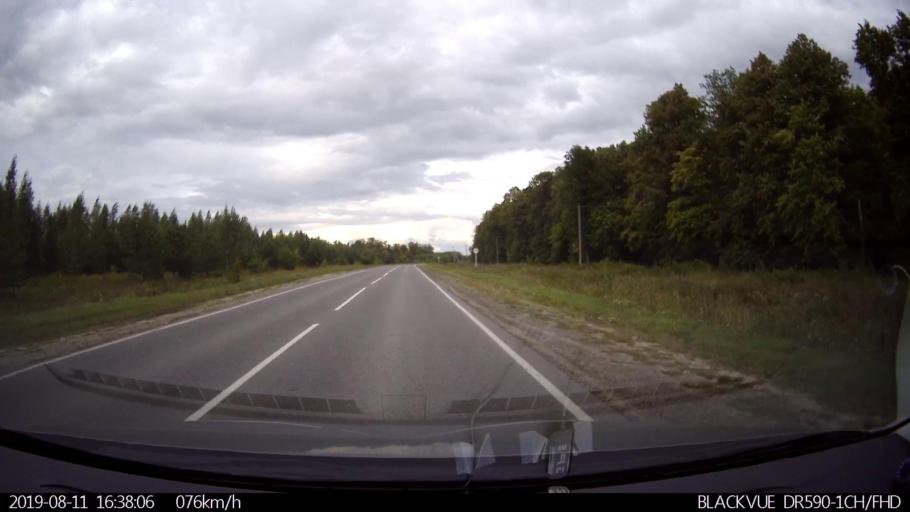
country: RU
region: Ulyanovsk
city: Mayna
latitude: 54.1324
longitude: 47.6206
